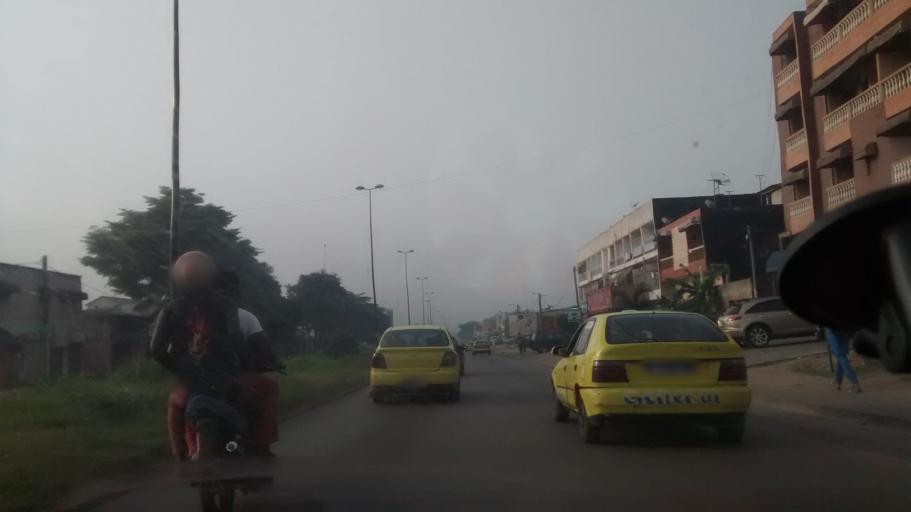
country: CI
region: Lagunes
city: Abobo
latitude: 5.4011
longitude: -3.9912
